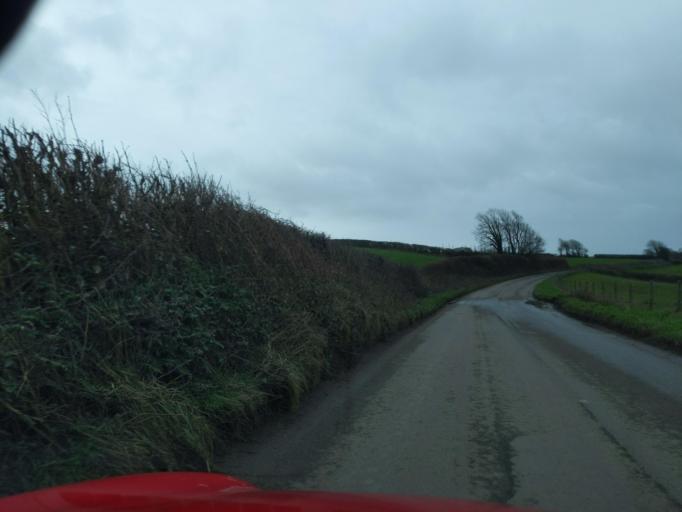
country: GB
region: England
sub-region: Devon
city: Modbury
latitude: 50.3348
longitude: -3.8690
